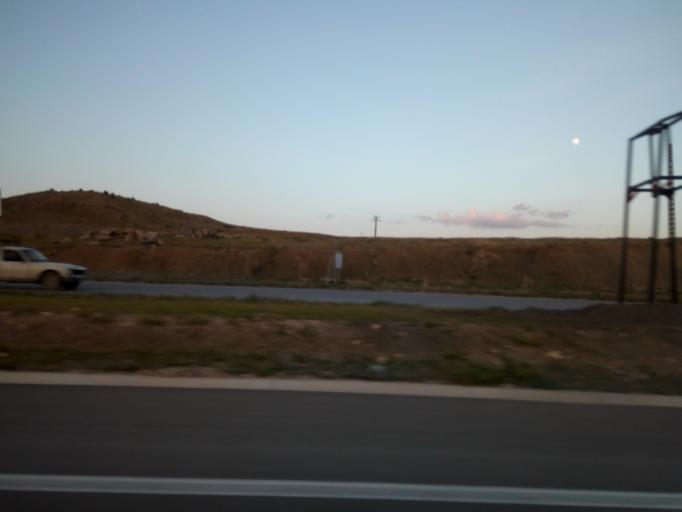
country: DZ
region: Medea
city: Ksar el Boukhari
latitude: 35.8313
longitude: 2.7710
